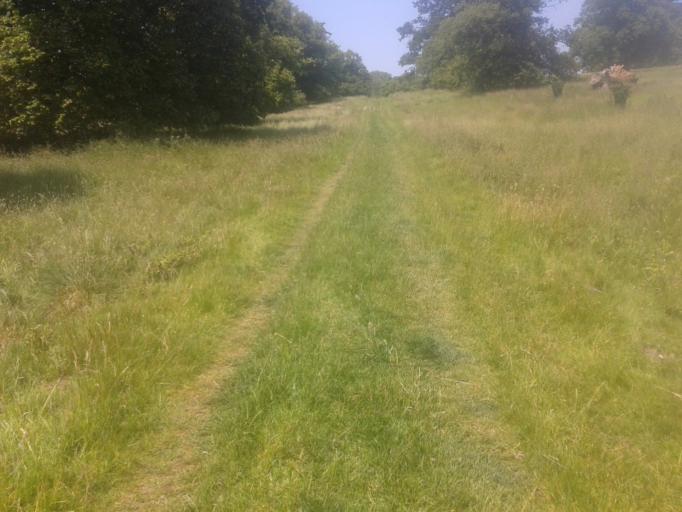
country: GB
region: England
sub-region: East Riding of Yorkshire
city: Londesborough
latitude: 53.8949
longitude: -0.6724
